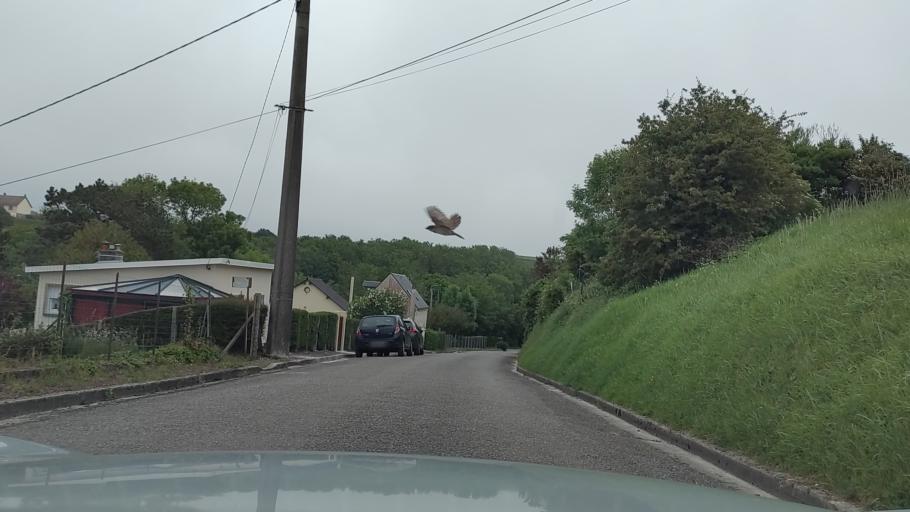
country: FR
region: Picardie
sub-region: Departement de la Somme
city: Ault
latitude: 50.0981
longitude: 1.4467
